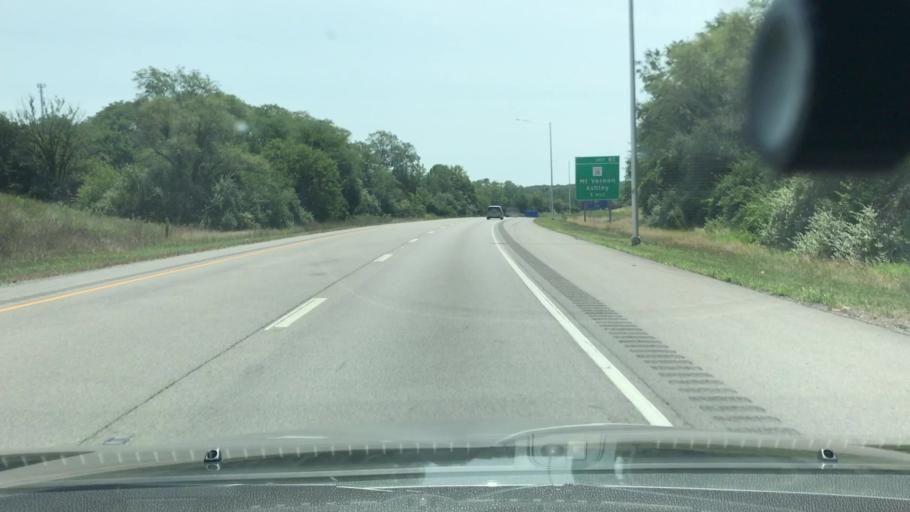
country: US
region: Illinois
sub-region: Jefferson County
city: Mount Vernon
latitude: 38.3367
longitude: -88.9591
